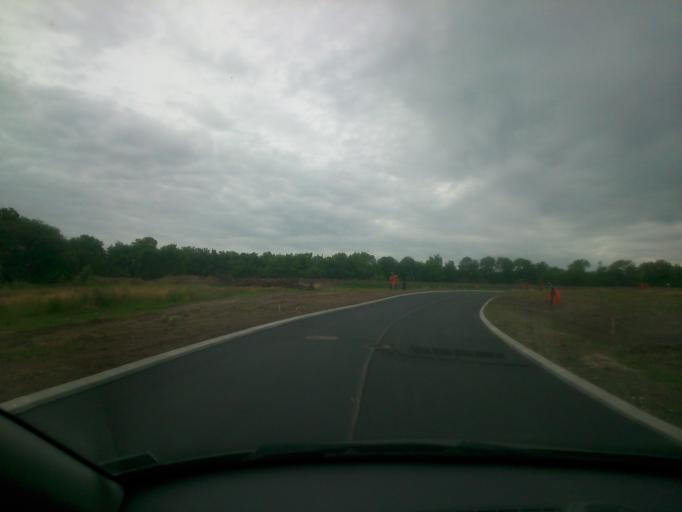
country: DK
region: South Denmark
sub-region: Esbjerg Kommune
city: Esbjerg
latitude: 55.5287
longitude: 8.4385
